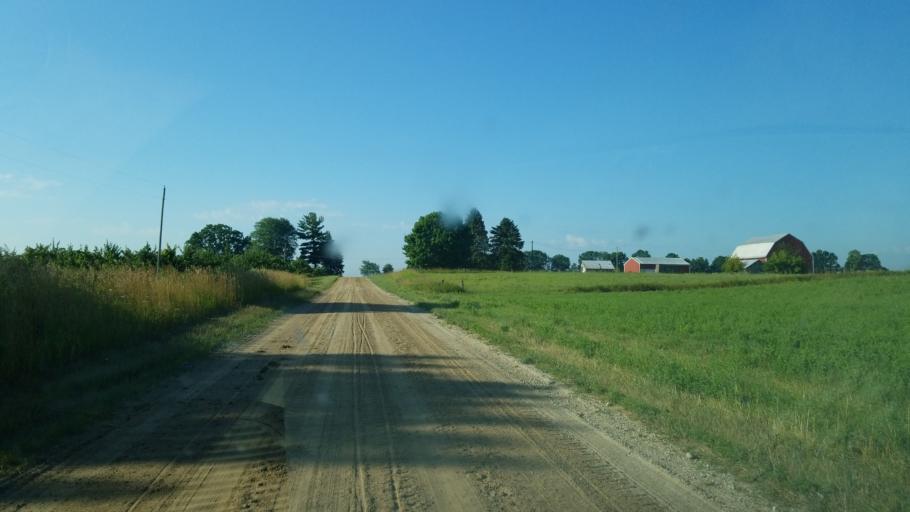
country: US
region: Michigan
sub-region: Mecosta County
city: Canadian Lakes
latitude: 43.5659
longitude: -85.3538
